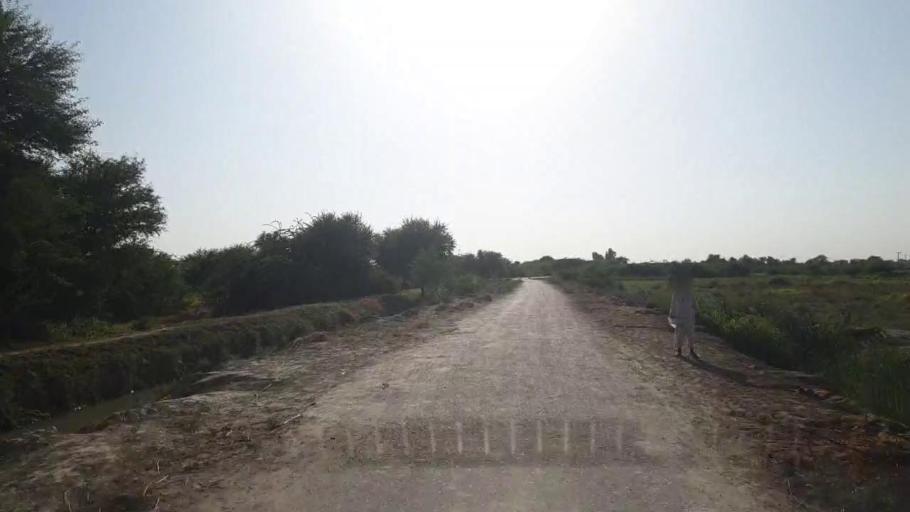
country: PK
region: Sindh
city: Badin
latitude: 24.5987
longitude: 68.9125
